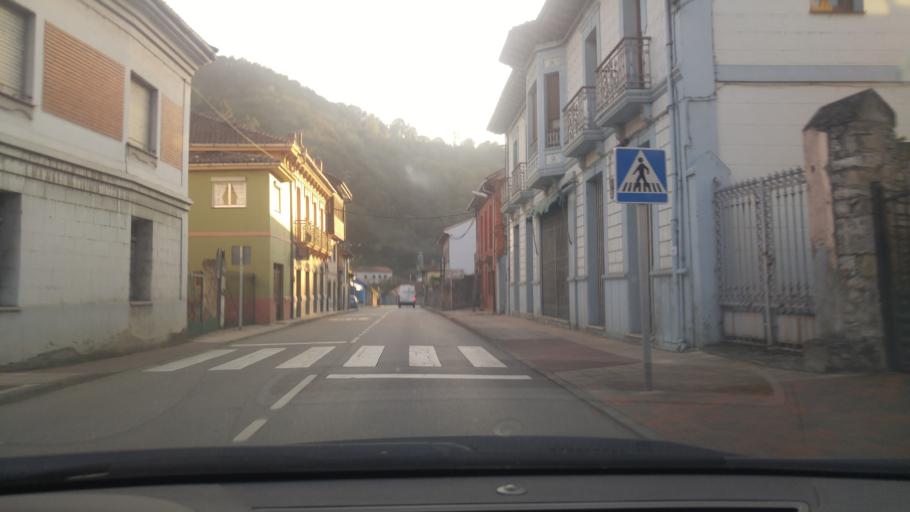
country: ES
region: Asturias
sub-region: Province of Asturias
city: Proaza
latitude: 43.2506
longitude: -6.0173
